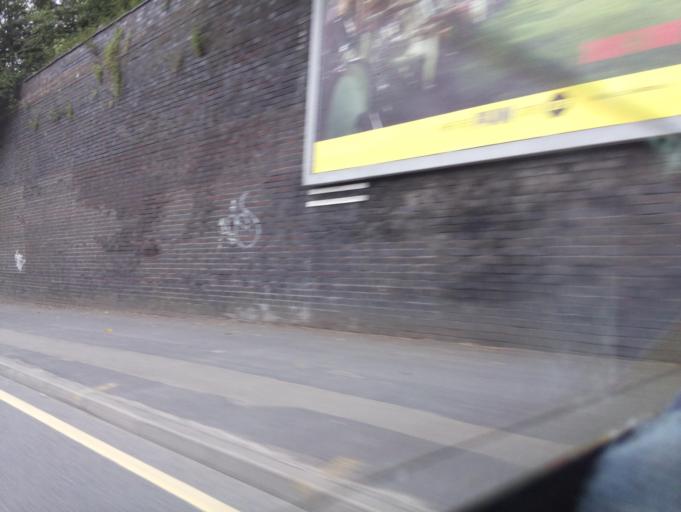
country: GB
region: England
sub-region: Wolverhampton
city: Wolverhampton
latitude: 52.5982
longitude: -2.1292
